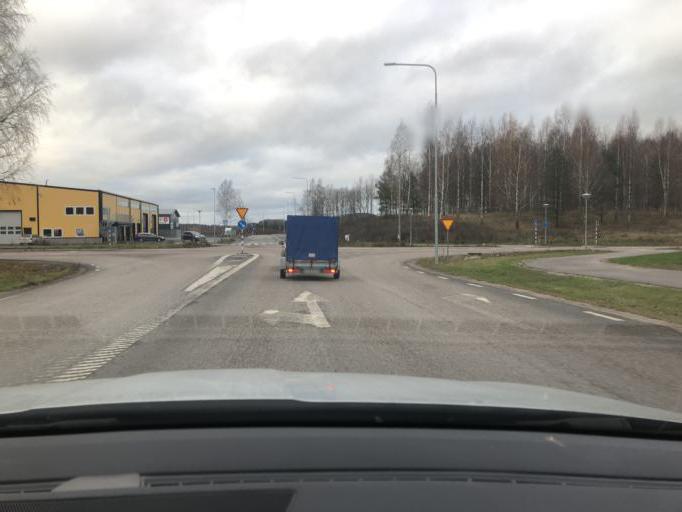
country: SE
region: Uppsala
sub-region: Tierps Kommun
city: Tierp
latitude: 60.3483
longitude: 17.4983
